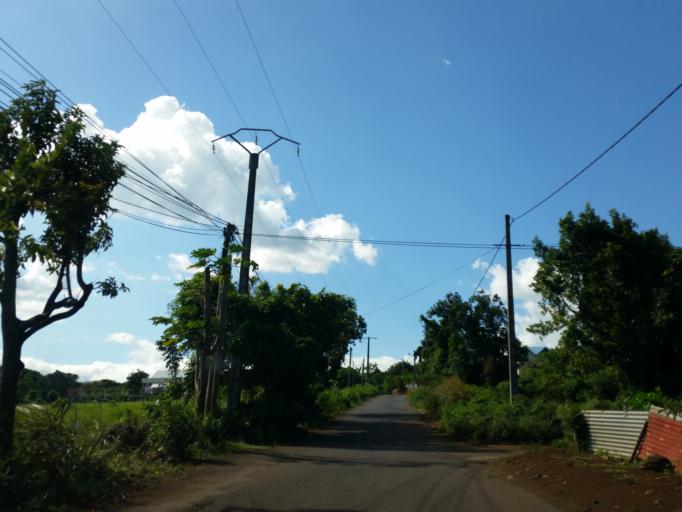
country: RE
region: Reunion
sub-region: Reunion
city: Saint-Pierre
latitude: -21.3227
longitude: 55.5009
